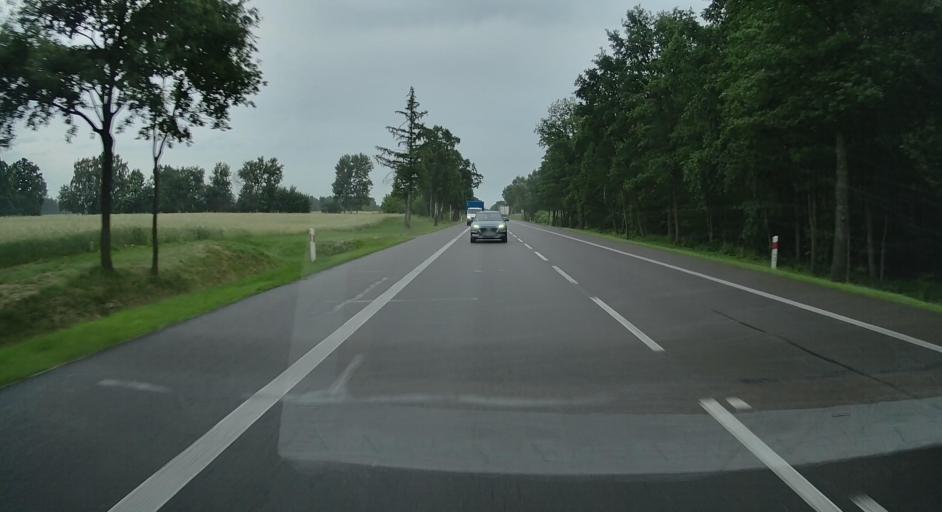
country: PL
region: Lublin Voivodeship
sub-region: Powiat bialski
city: Miedzyrzec Podlaski
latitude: 52.0124
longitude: 22.8382
